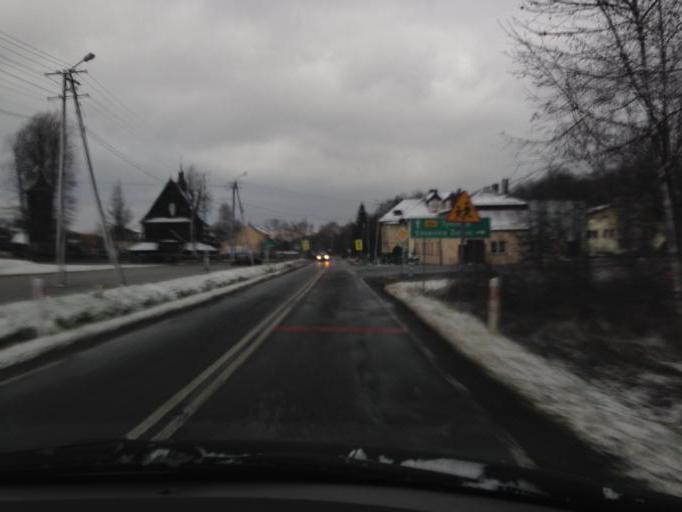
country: PL
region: Lesser Poland Voivodeship
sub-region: Powiat brzeski
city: Gnojnik
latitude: 49.8514
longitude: 20.6191
